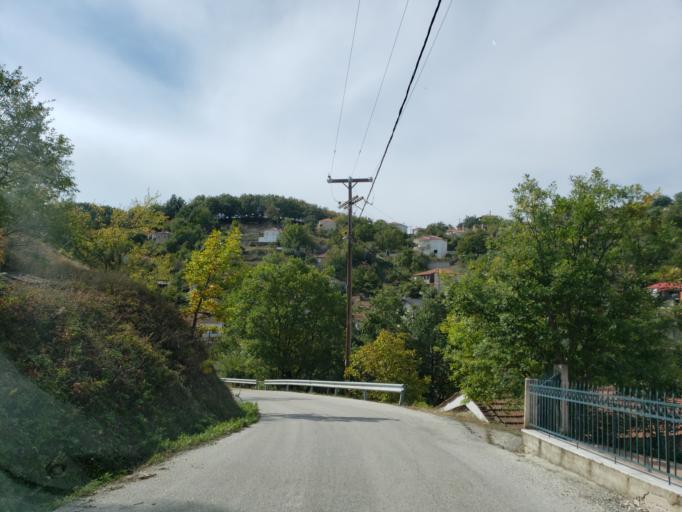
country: GR
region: Thessaly
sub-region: Trikala
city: Kastraki
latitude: 39.7744
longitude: 21.6603
